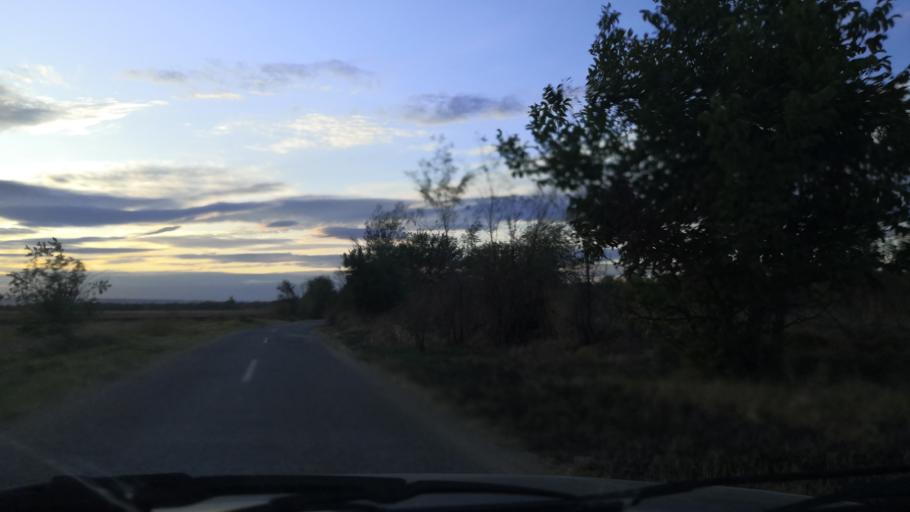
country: RO
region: Mehedinti
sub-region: Comuna Gruia
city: Izvoarele
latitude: 44.2767
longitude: 22.6569
